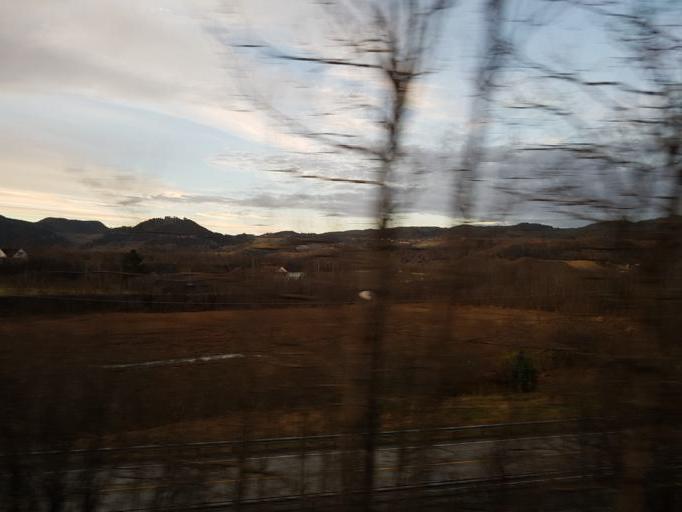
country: NO
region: Sor-Trondelag
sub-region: Melhus
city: Lundamo
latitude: 63.2186
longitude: 10.2939
